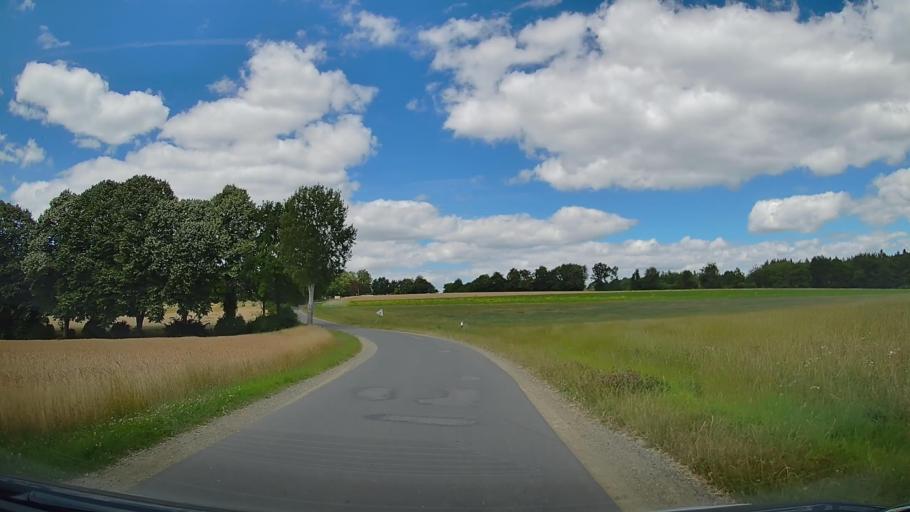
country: DE
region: Lower Saxony
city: Belm
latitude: 52.3843
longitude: 8.1362
